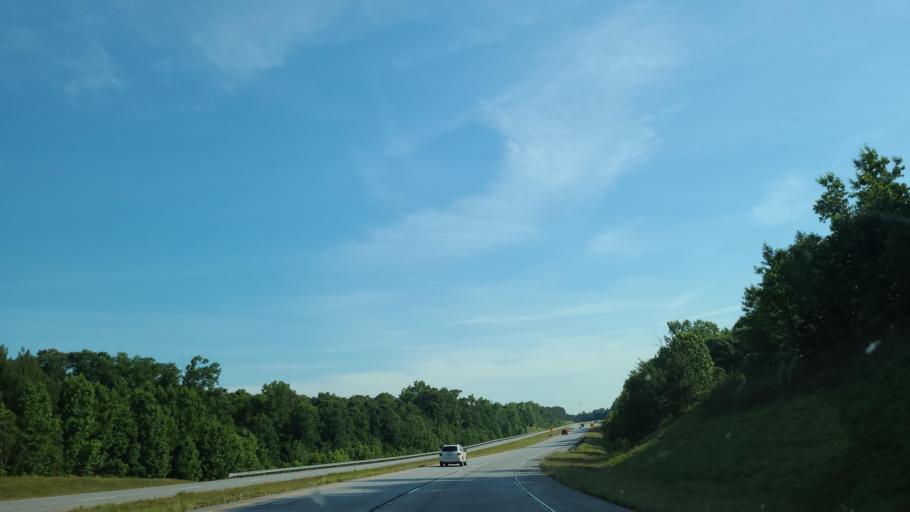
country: US
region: Georgia
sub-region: Jackson County
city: Nicholson
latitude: 34.0652
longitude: -83.4259
